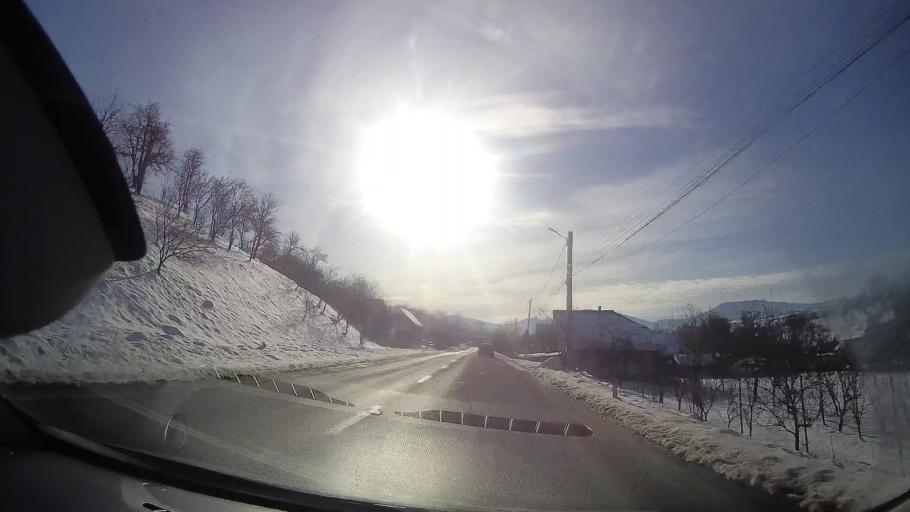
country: RO
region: Neamt
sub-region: Comuna Baltatesti
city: Valea Seaca
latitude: 47.1292
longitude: 26.3146
